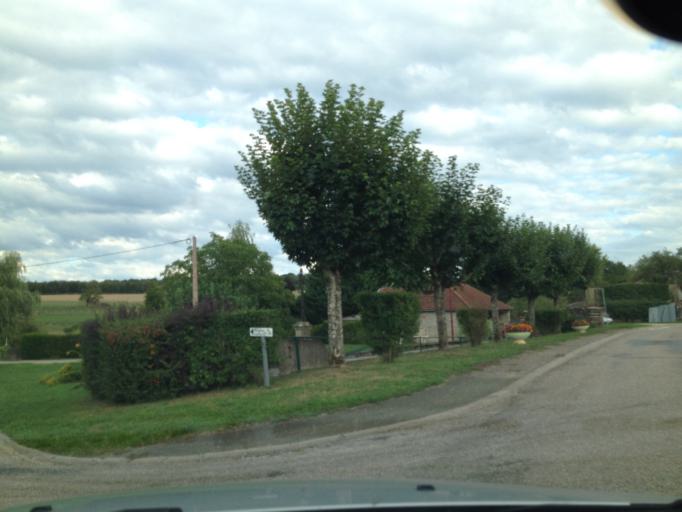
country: FR
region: Lorraine
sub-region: Departement des Vosges
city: Darney
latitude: 47.9456
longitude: 6.1004
